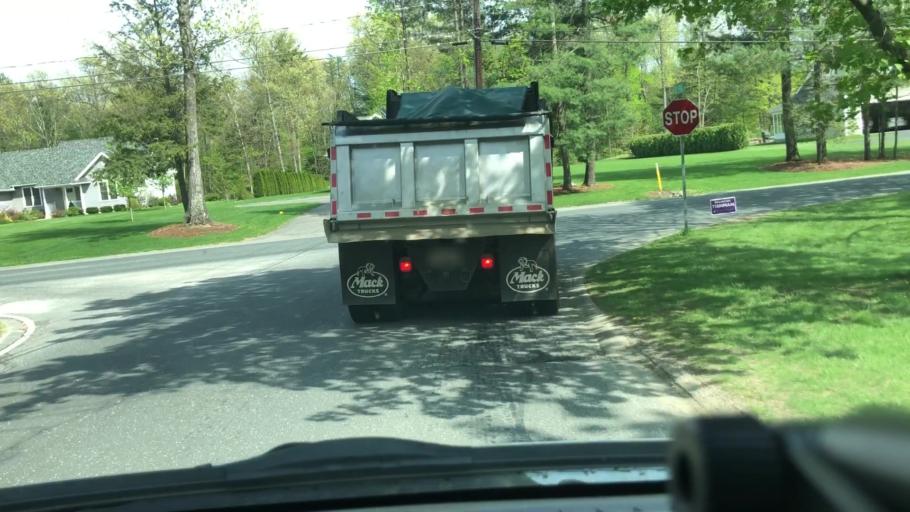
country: US
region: Massachusetts
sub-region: Hampshire County
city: Southampton
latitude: 42.2557
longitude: -72.7200
